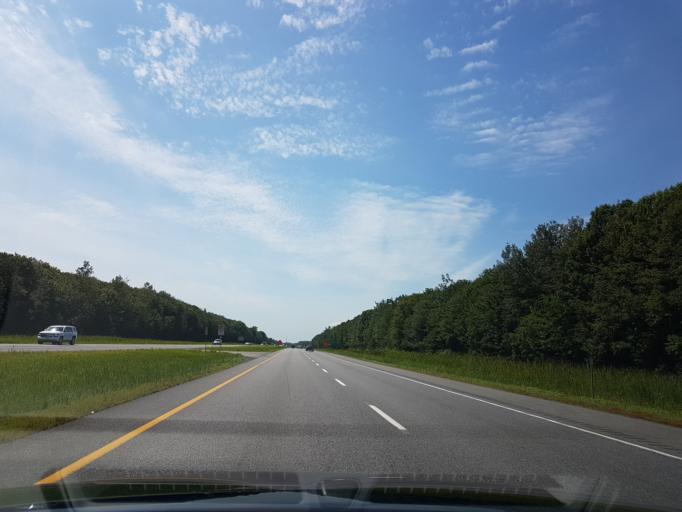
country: CA
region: Quebec
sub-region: Monteregie
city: Salaberry-de-Valleyfield
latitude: 45.3203
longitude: -74.1371
